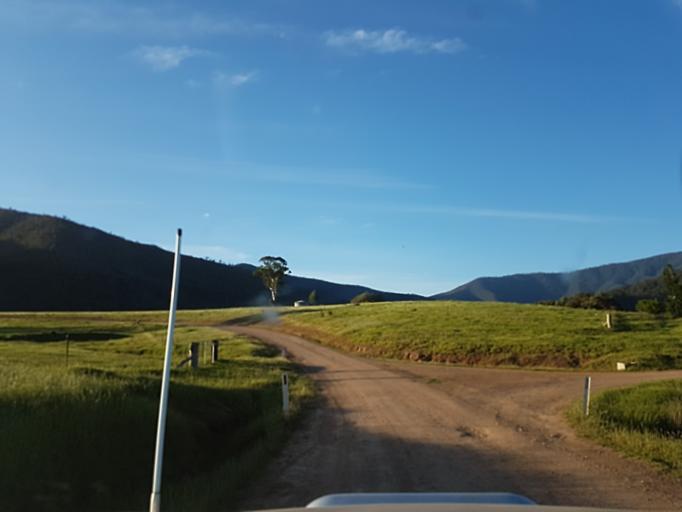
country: AU
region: Victoria
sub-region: East Gippsland
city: Bairnsdale
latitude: -37.4014
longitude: 147.1040
